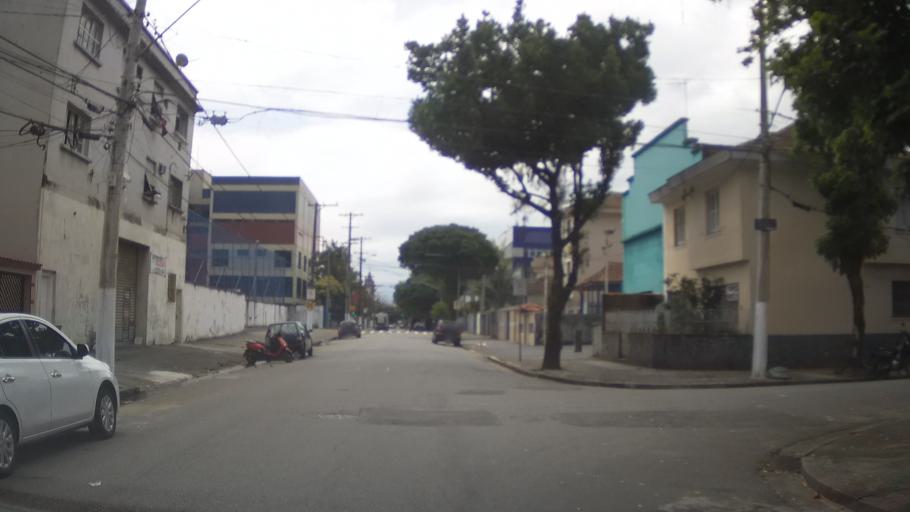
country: BR
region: Sao Paulo
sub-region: Santos
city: Santos
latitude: -23.9590
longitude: -46.3162
